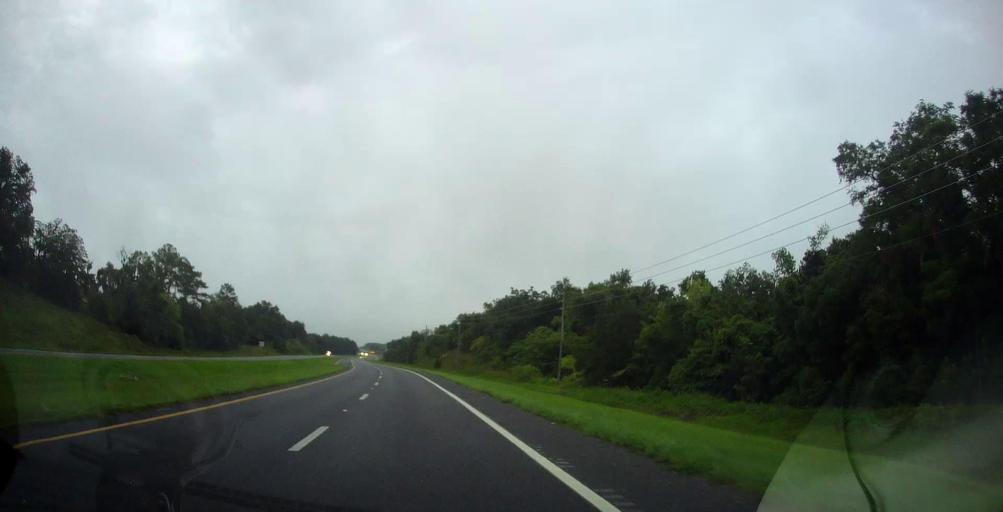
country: US
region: Florida
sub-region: Marion County
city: Ocala
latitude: 29.2599
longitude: -82.1639
